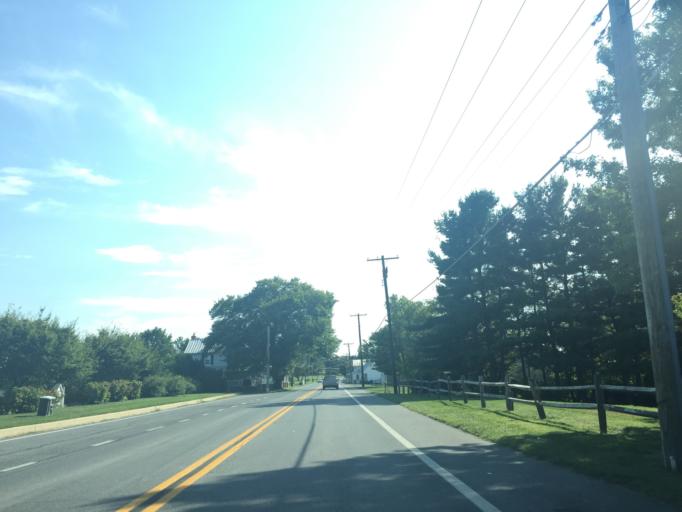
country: US
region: Maryland
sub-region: Carroll County
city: Mount Airy
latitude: 39.3888
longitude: -77.1434
